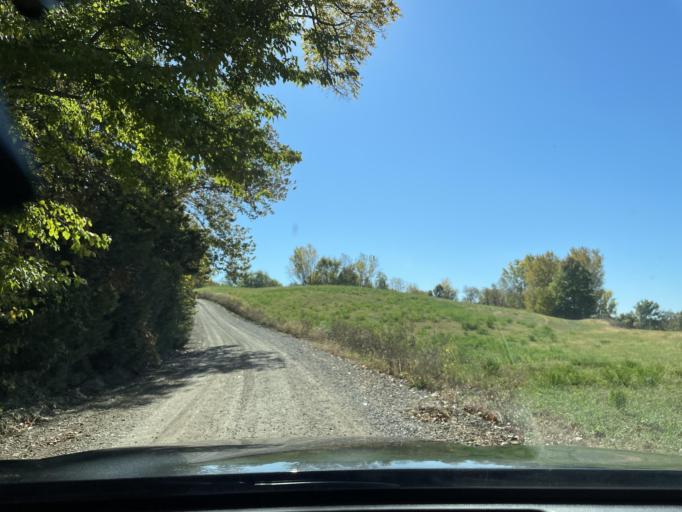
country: US
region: Missouri
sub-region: Andrew County
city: Savannah
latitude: 39.9367
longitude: -94.8639
